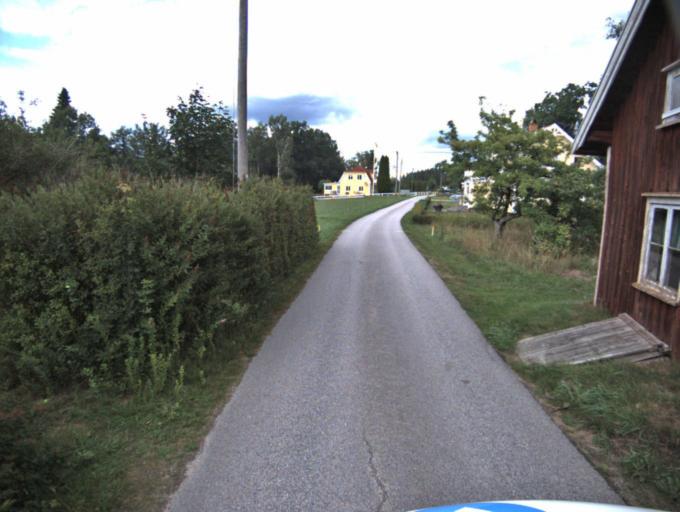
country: SE
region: Vaestra Goetaland
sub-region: Ulricehamns Kommun
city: Ulricehamn
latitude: 57.6811
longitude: 13.3841
